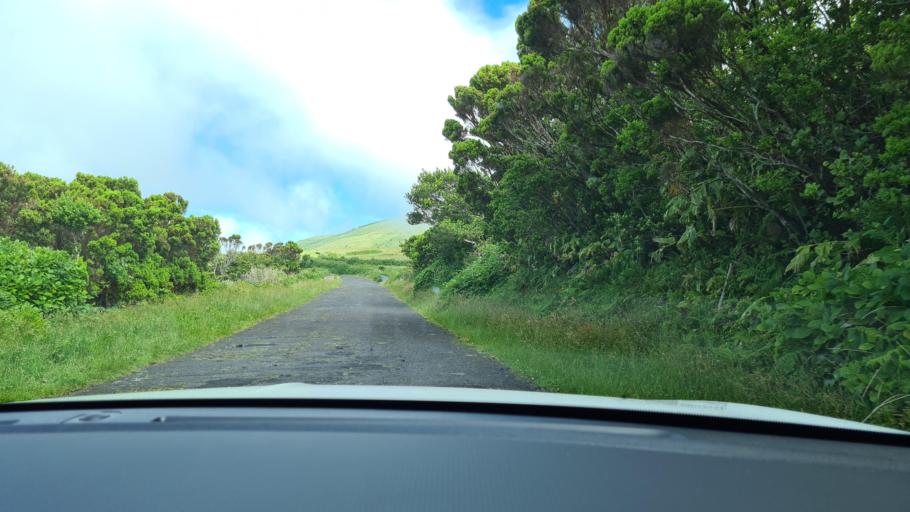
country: PT
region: Azores
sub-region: Sao Roque do Pico
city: Sao Roque do Pico
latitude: 38.6694
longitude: -28.1314
